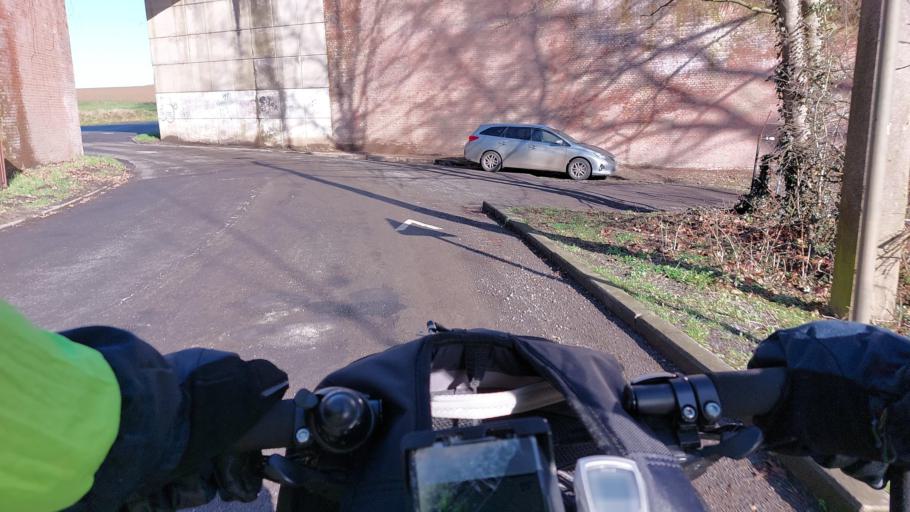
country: BE
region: Wallonia
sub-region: Province du Hainaut
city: Ecaussinnes-d'Enghien
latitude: 50.5752
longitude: 4.1754
